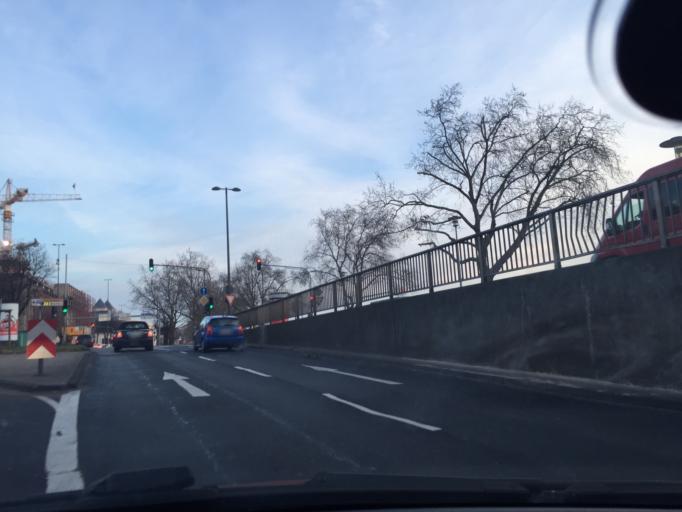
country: DE
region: North Rhine-Westphalia
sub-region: Regierungsbezirk Koln
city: Altstadt Nord
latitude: 50.9419
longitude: 6.9625
